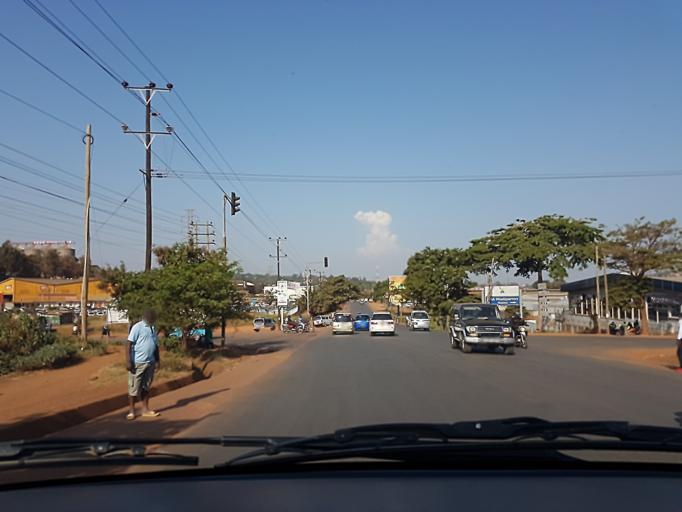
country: UG
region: Central Region
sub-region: Wakiso District
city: Kireka
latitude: 0.3335
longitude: 32.6176
